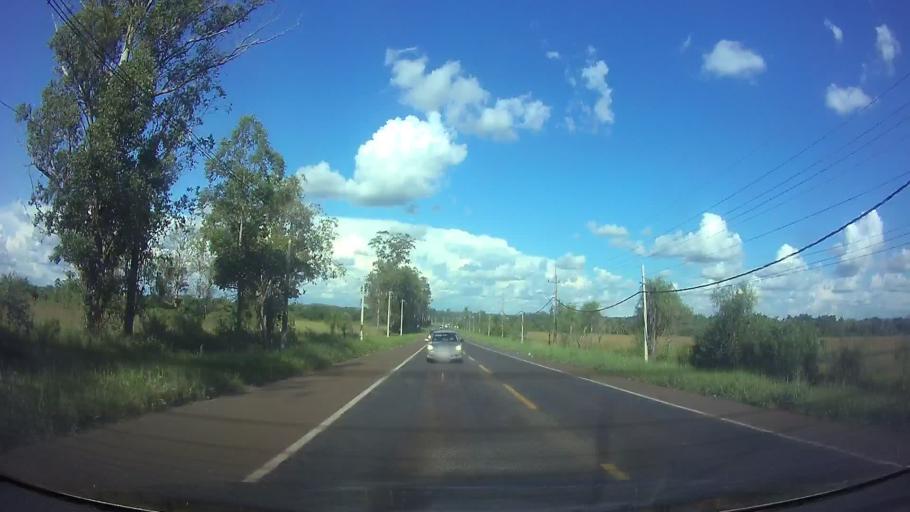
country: PY
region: Cordillera
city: Eusebio Ayala
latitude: -25.3808
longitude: -56.9936
